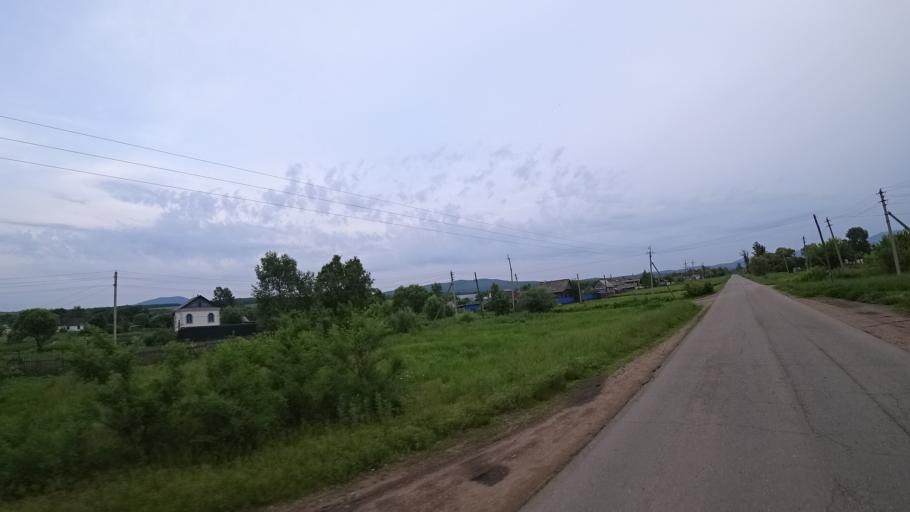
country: RU
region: Primorskiy
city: Novosysoyevka
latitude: 44.2377
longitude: 133.3693
